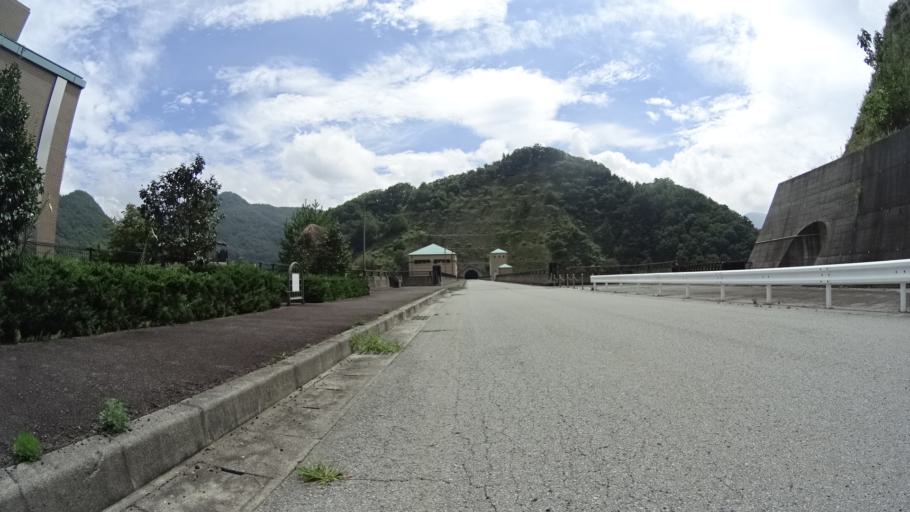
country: JP
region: Yamanashi
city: Nirasaki
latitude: 35.8596
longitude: 138.4969
